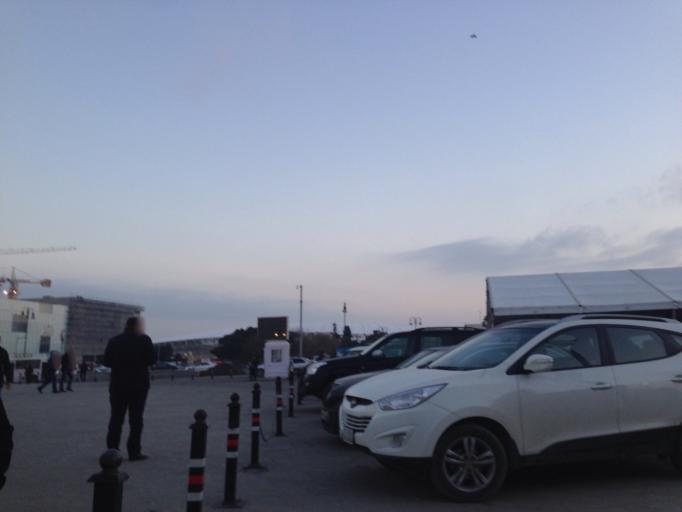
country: AZ
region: Baki
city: Baku
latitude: 40.4009
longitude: 49.8500
